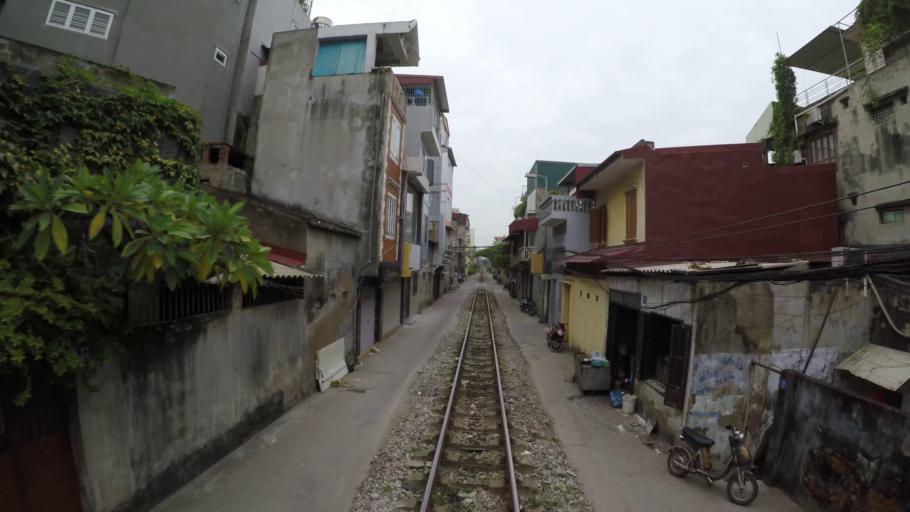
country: VN
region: Hai Phong
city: Haiphong
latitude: 20.8668
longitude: 106.6571
